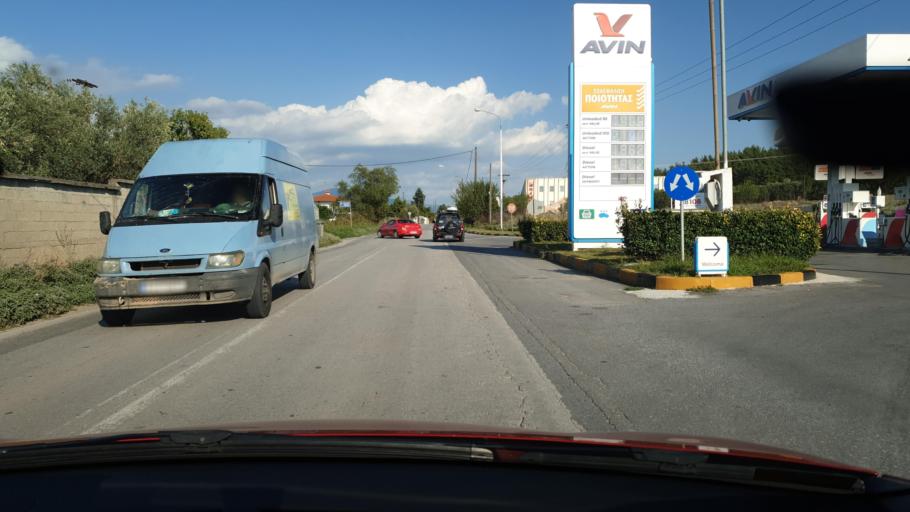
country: GR
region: Central Macedonia
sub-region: Nomos Thessalonikis
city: Neo Rysi
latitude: 40.4948
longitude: 23.0092
